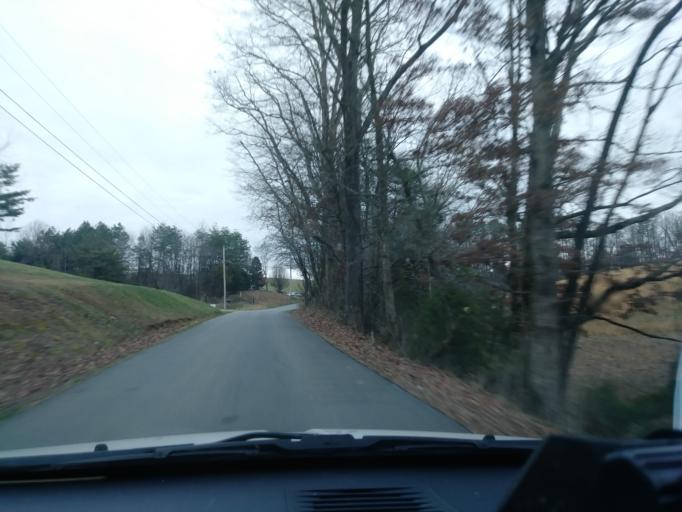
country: US
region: Tennessee
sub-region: Greene County
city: Greeneville
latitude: 36.0775
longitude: -82.8870
